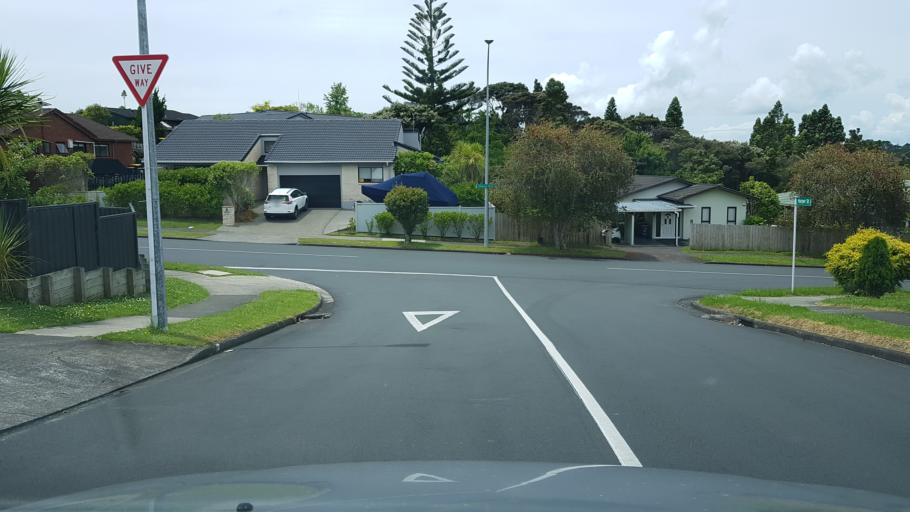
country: NZ
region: Auckland
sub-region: Auckland
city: North Shore
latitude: -36.8172
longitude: 174.7097
